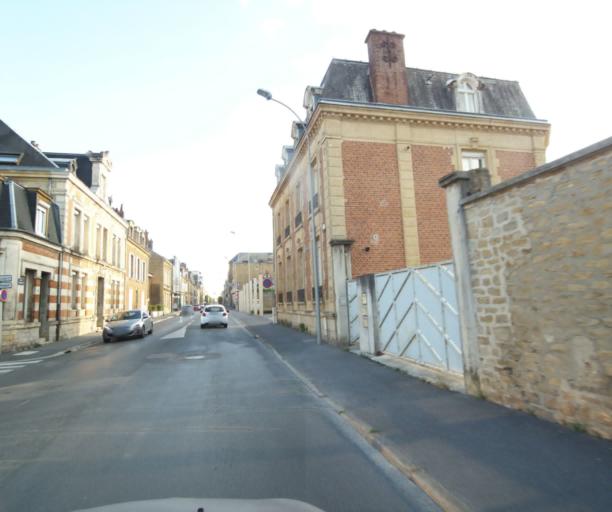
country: FR
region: Champagne-Ardenne
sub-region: Departement des Ardennes
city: Charleville-Mezieres
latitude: 49.7743
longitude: 4.7271
